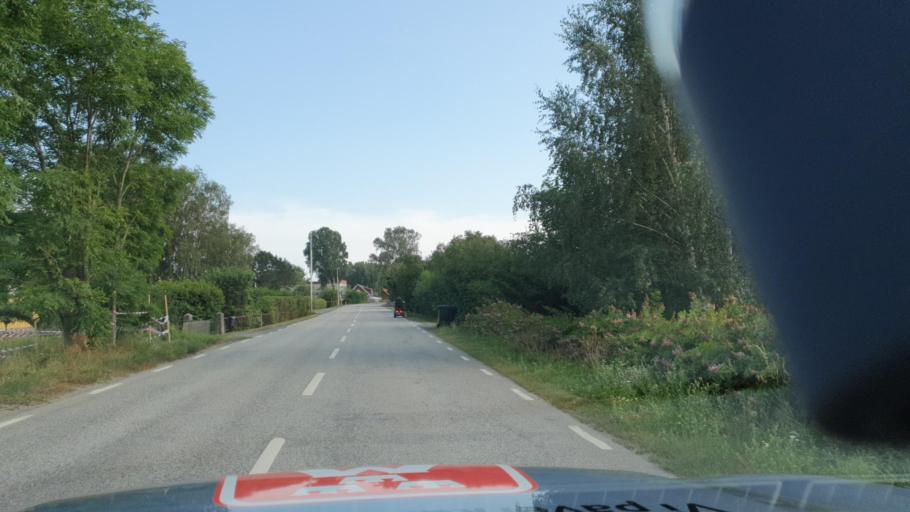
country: SE
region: Blekinge
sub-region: Solvesborgs Kommun
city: Soelvesborg
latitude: 56.0441
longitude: 14.6875
